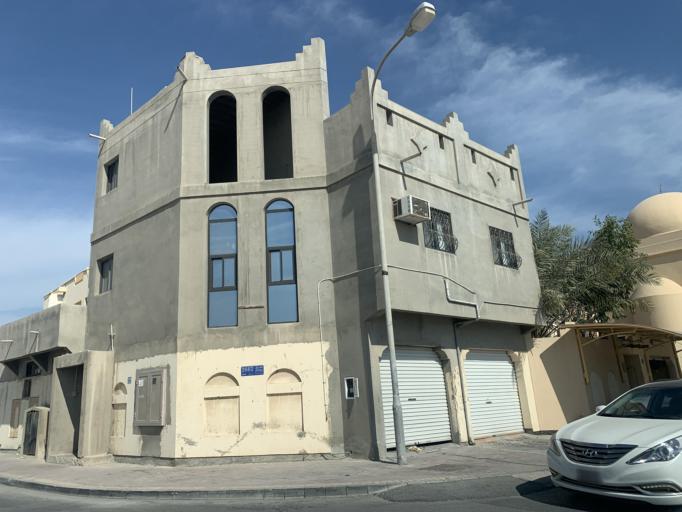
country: BH
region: Central Governorate
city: Madinat Hamad
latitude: 26.1157
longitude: 50.4857
